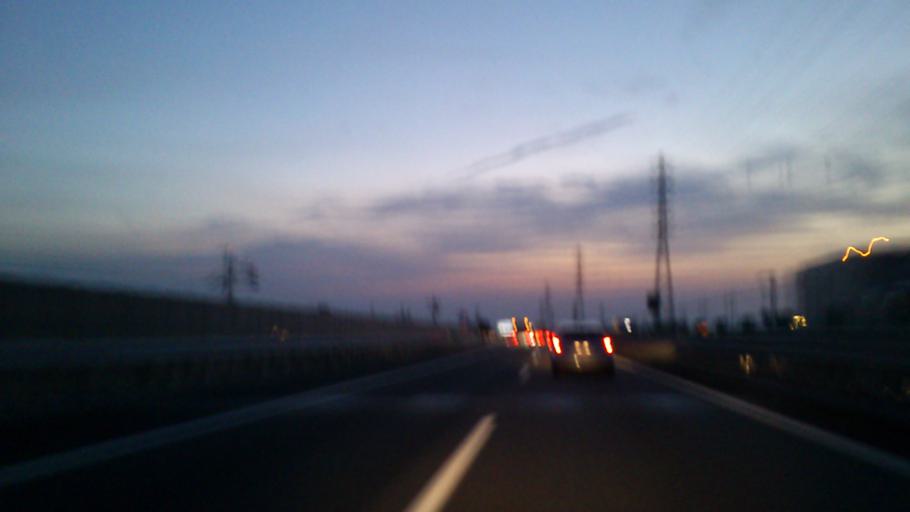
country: JP
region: Aichi
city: Komaki
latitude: 35.2963
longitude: 136.9362
